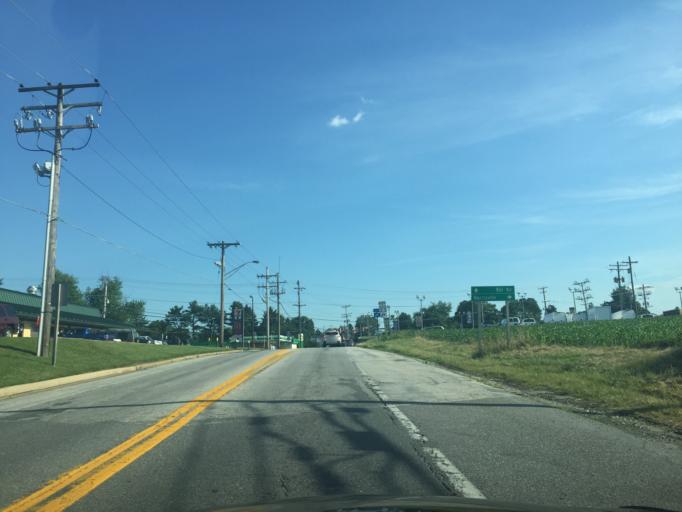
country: US
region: Maryland
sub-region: Harford County
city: Jarrettsville
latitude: 39.6059
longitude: -76.4778
